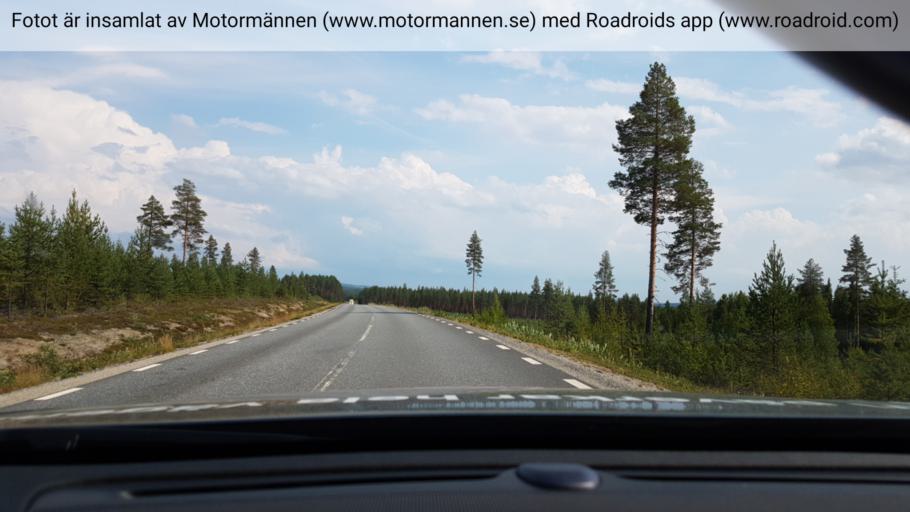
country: SE
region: Vaesterbotten
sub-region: Lycksele Kommun
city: Lycksele
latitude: 64.3944
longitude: 19.0762
